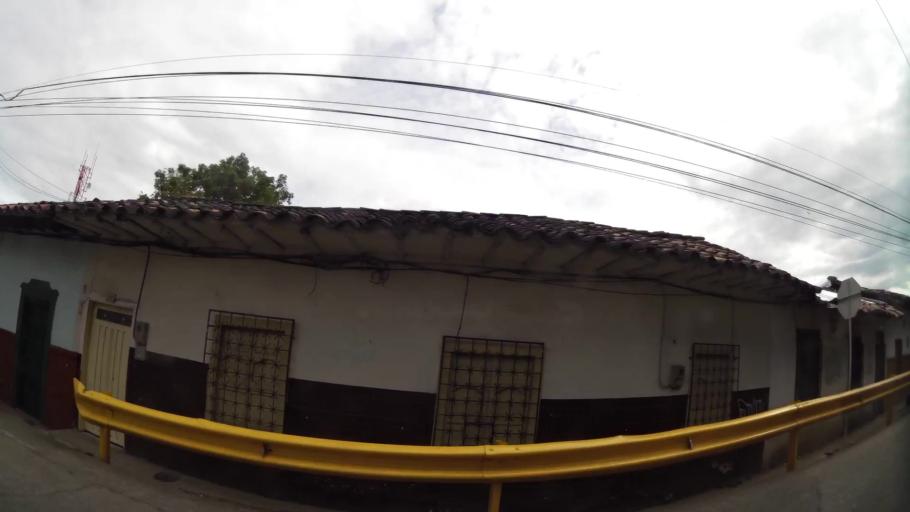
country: CO
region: Antioquia
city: Rionegro
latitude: 6.1521
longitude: -75.3790
